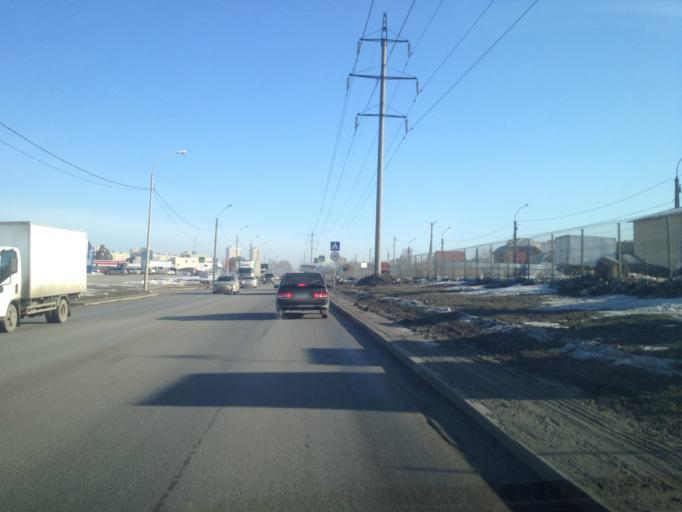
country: RU
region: Sverdlovsk
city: Sovkhoznyy
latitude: 56.7585
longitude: 60.5881
